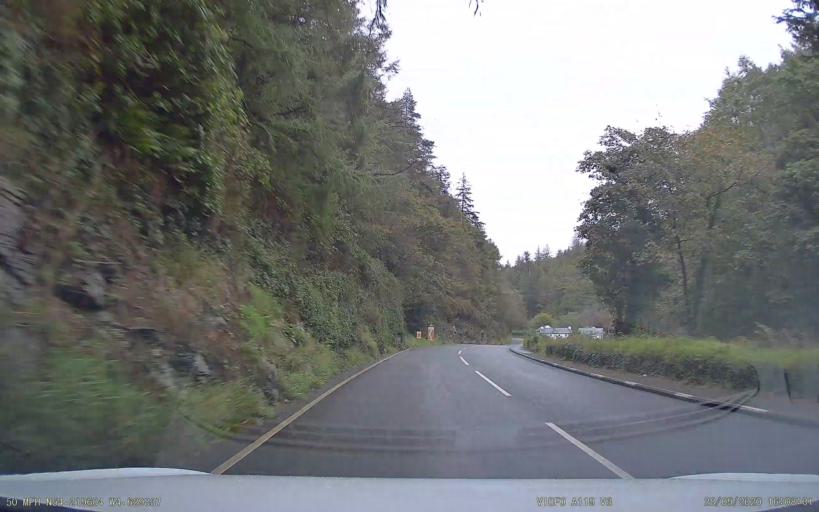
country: IM
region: Castletown
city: Castletown
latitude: 54.2196
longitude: -4.6298
